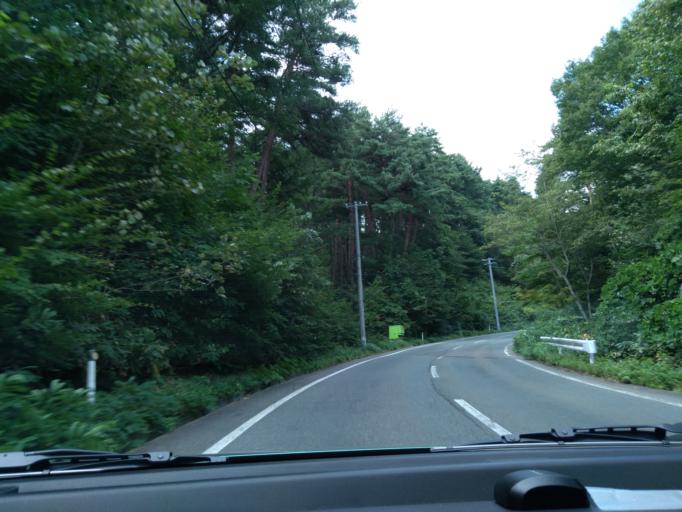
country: JP
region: Iwate
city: Morioka-shi
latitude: 39.6327
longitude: 141.0838
